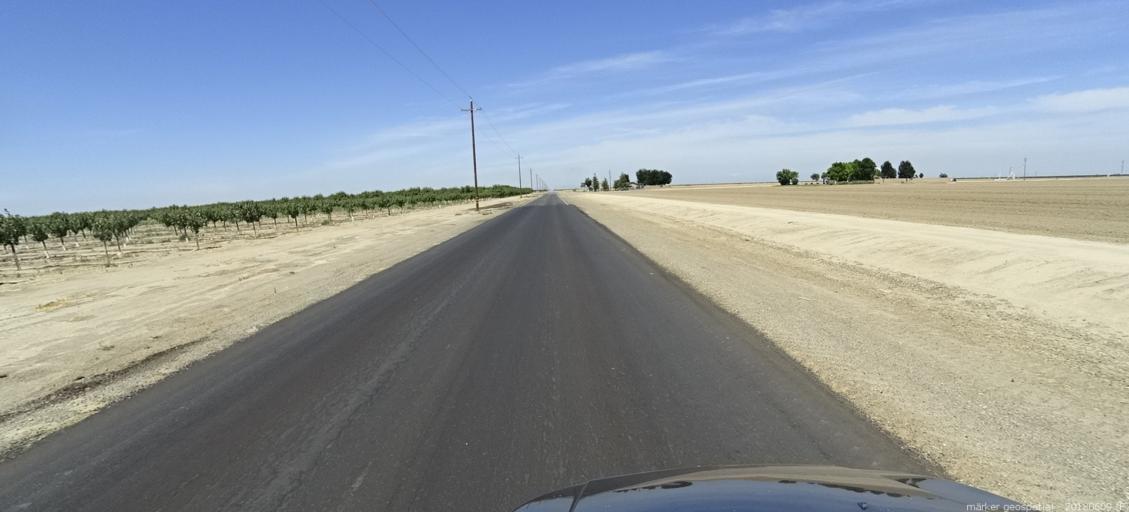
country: US
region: California
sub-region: Madera County
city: Fairmead
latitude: 36.9527
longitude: -120.2978
